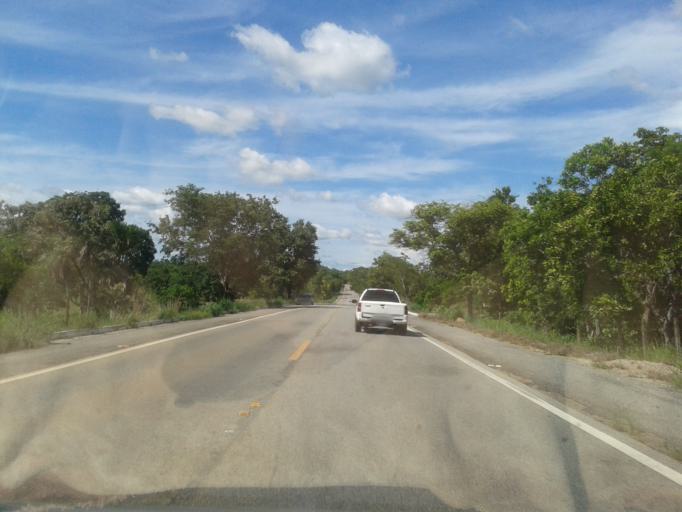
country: BR
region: Goias
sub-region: Itapuranga
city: Itapuranga
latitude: -15.3810
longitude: -50.3892
